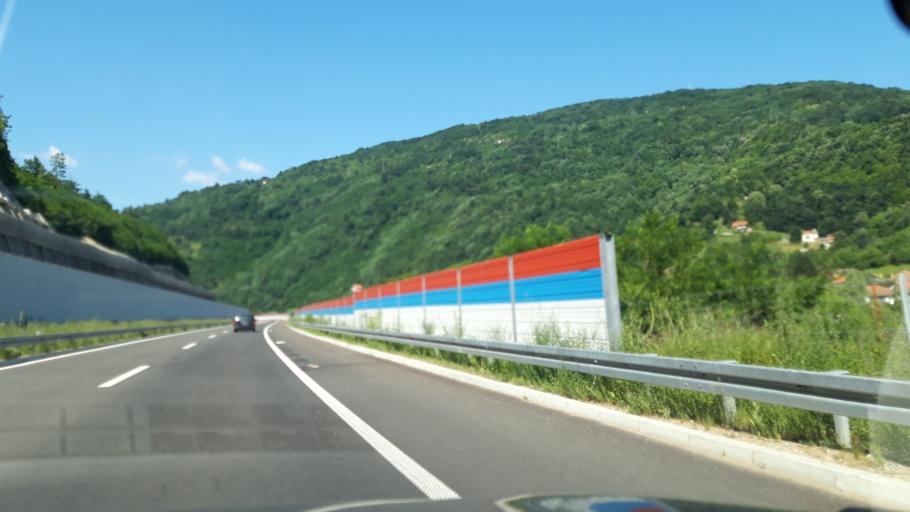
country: RS
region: Central Serbia
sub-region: Pcinjski Okrug
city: Vladicin Han
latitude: 42.7754
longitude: 22.0877
